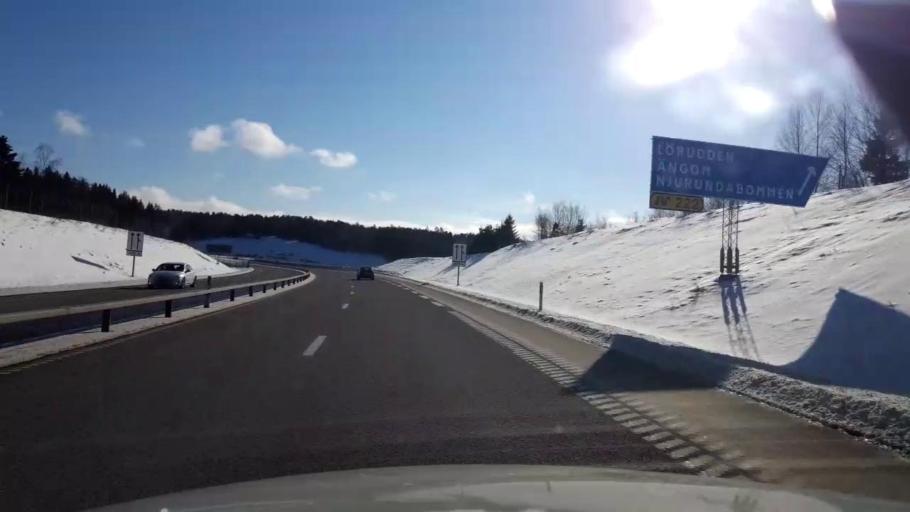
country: SE
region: Vaesternorrland
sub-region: Sundsvalls Kommun
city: Nolby
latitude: 62.2701
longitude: 17.3458
